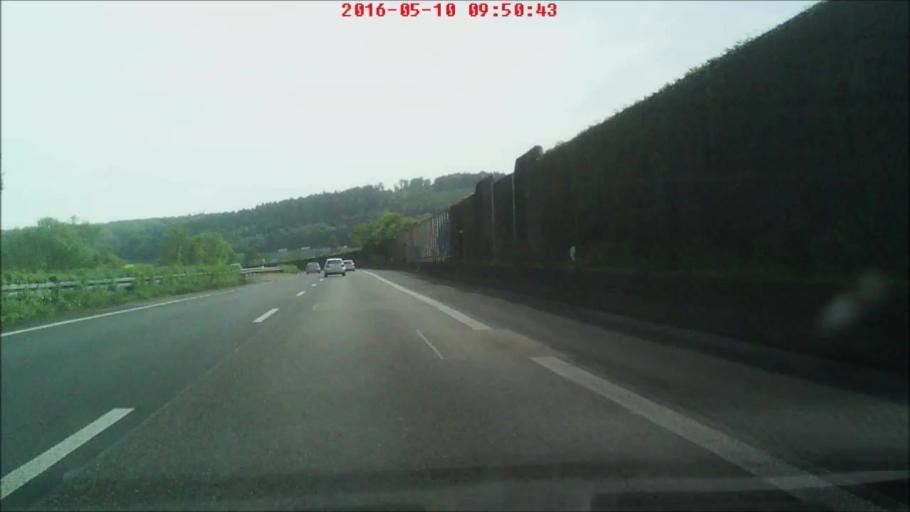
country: DE
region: Hesse
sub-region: Regierungsbezirk Darmstadt
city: Wachtersbach
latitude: 50.2244
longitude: 9.2627
